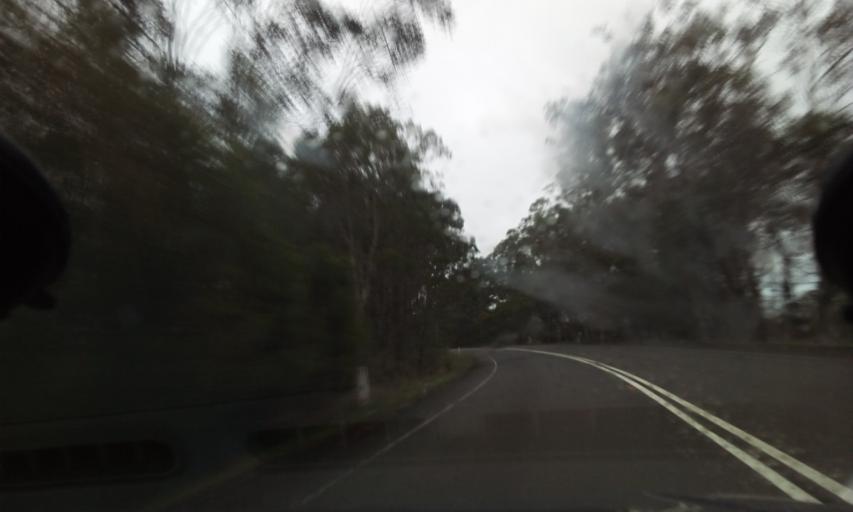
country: AU
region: New South Wales
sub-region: Wollondilly
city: Douglas Park
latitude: -34.2639
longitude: 150.7186
